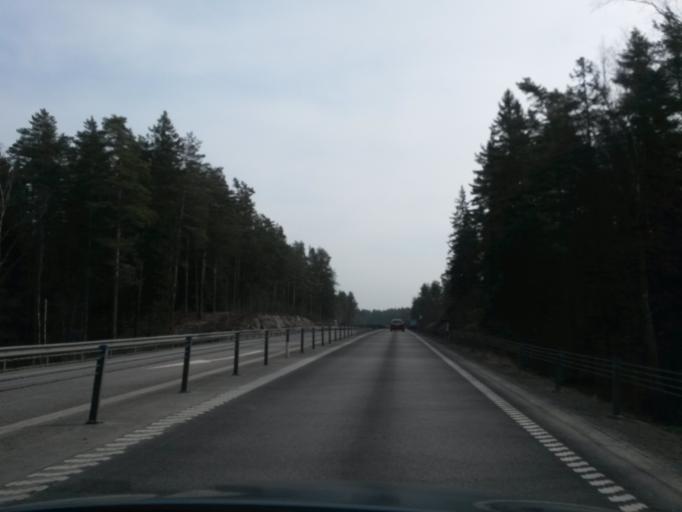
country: SE
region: OErebro
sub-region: Laxa Kommun
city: Laxa
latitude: 58.9757
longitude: 14.5711
